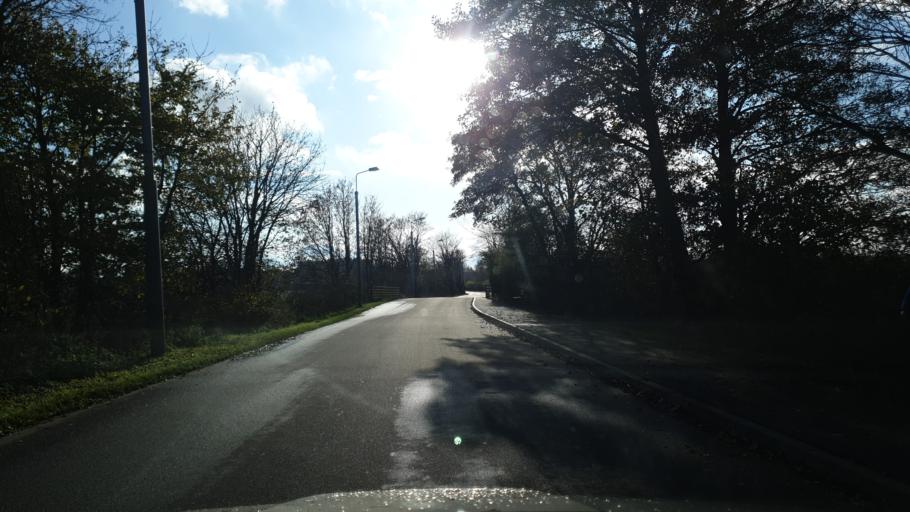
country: PL
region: Pomeranian Voivodeship
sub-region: Powiat pucki
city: Jastrzebia Gora
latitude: 54.8291
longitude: 18.2444
